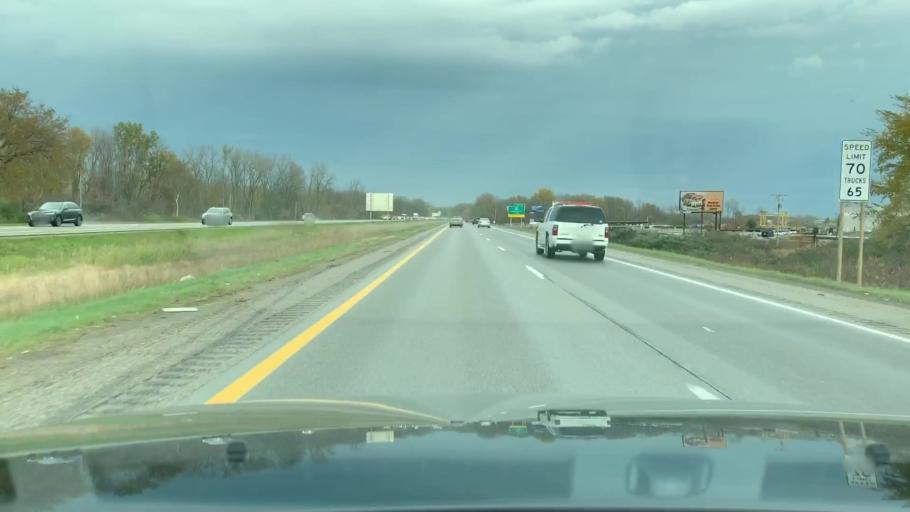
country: US
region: Michigan
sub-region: Kent County
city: Grandville
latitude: 42.9226
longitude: -85.7542
